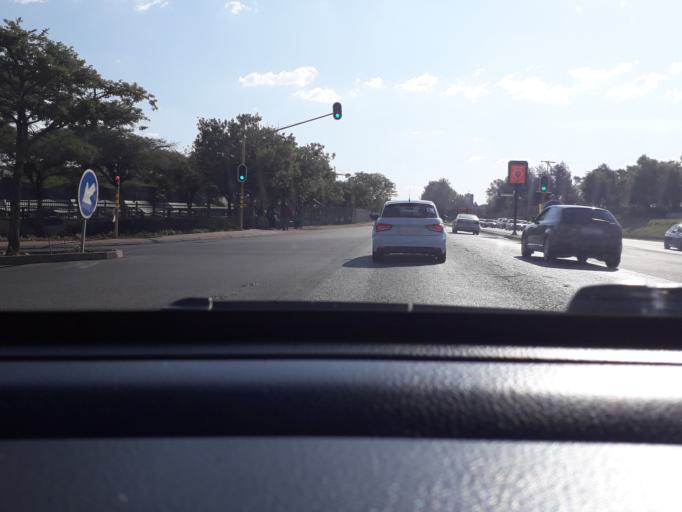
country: ZA
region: Gauteng
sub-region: City of Johannesburg Metropolitan Municipality
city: Midrand
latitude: -26.0424
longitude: 28.0987
